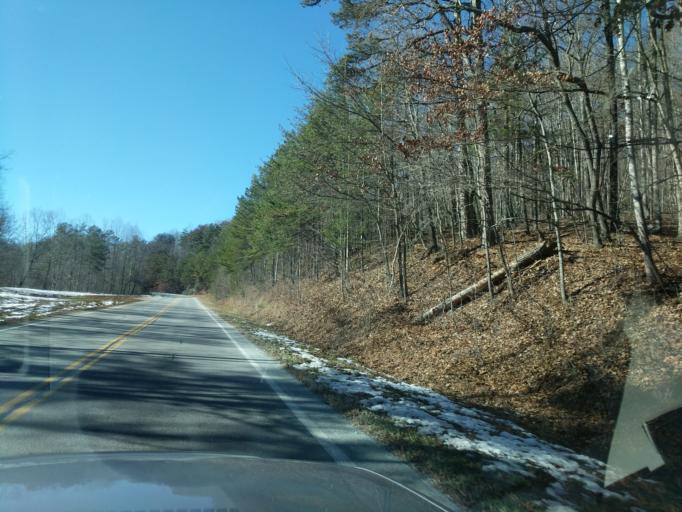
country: US
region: Georgia
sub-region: Rabun County
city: Clayton
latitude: 34.8739
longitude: -83.5523
